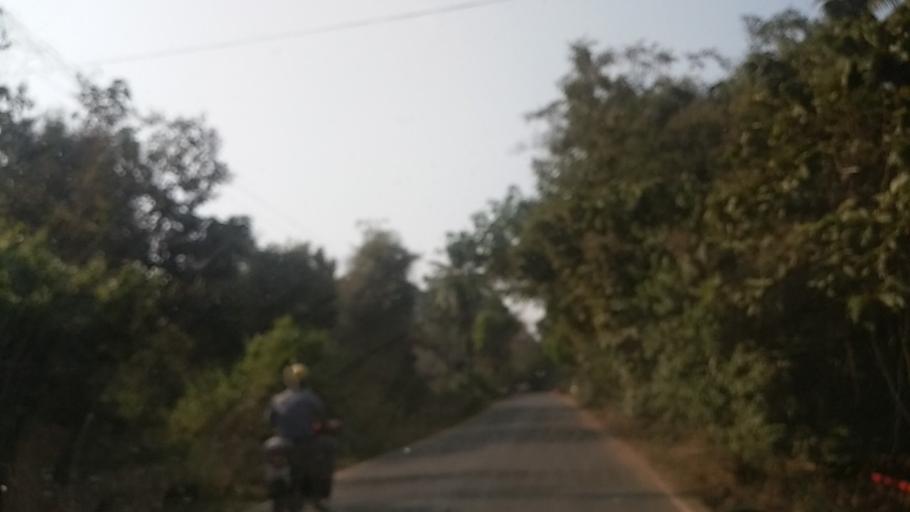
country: IN
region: Goa
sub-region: North Goa
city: Pernem
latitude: 15.7143
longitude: 73.8068
